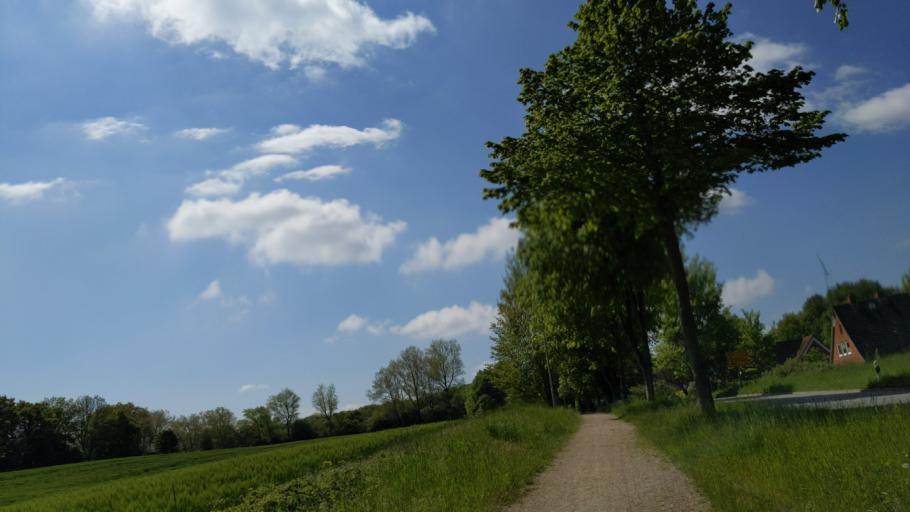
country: DE
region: Schleswig-Holstein
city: Eutin
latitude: 54.1841
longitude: 10.6151
